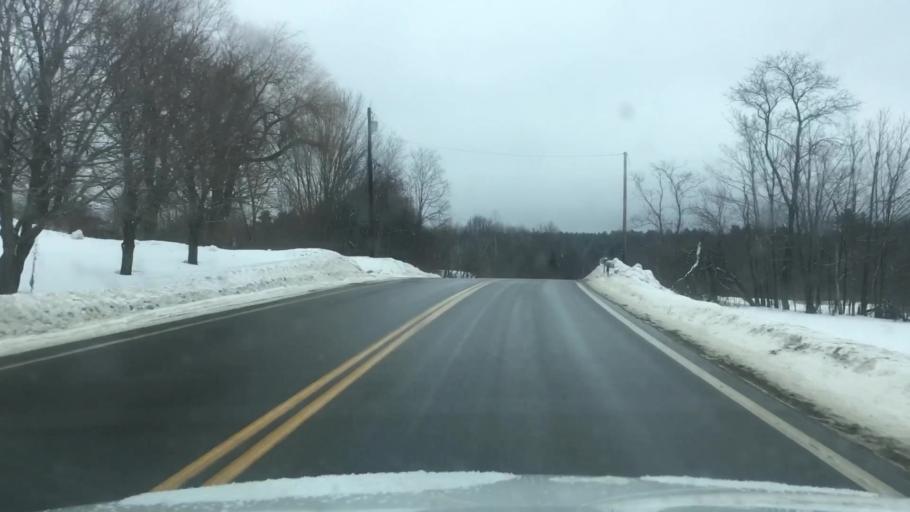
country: US
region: Maine
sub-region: Franklin County
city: Chesterville
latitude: 44.5921
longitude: -70.1452
